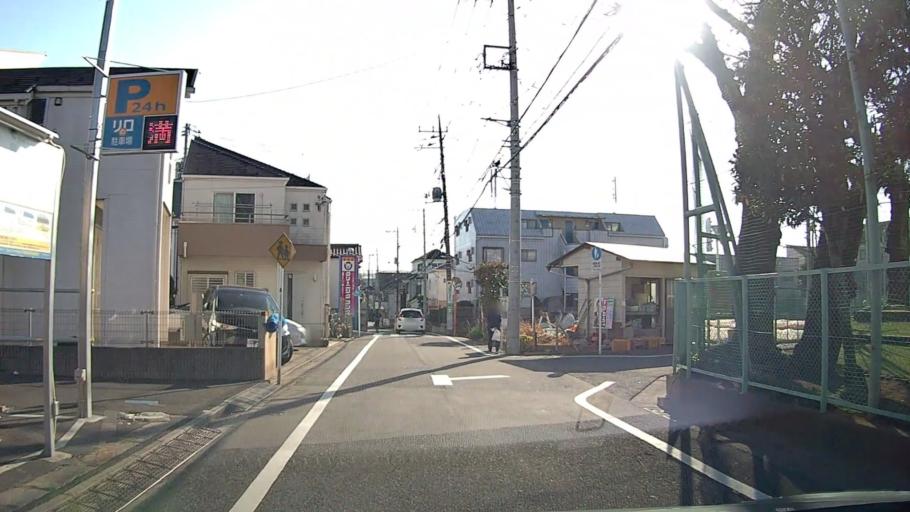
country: JP
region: Saitama
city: Wako
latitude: 35.7652
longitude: 139.5939
